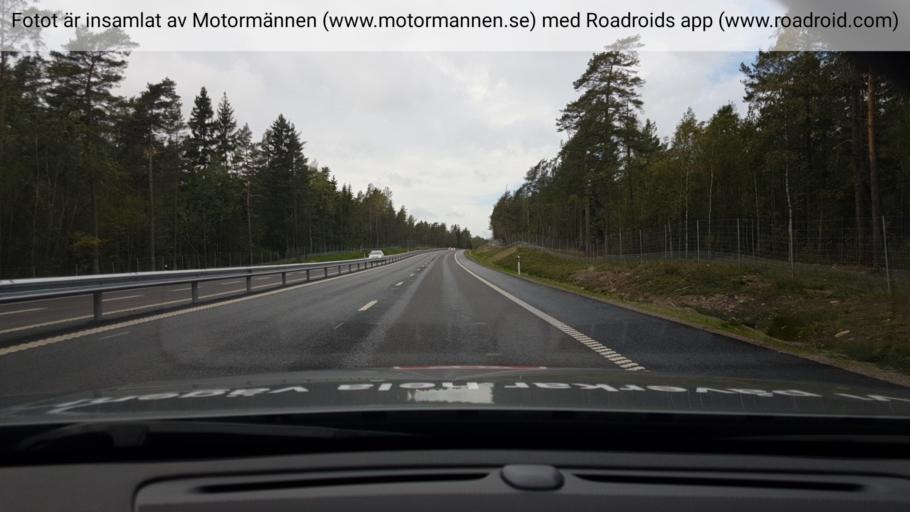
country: SE
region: Vaermland
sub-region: Hammaro Kommun
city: Skoghall
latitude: 59.3810
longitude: 13.4003
